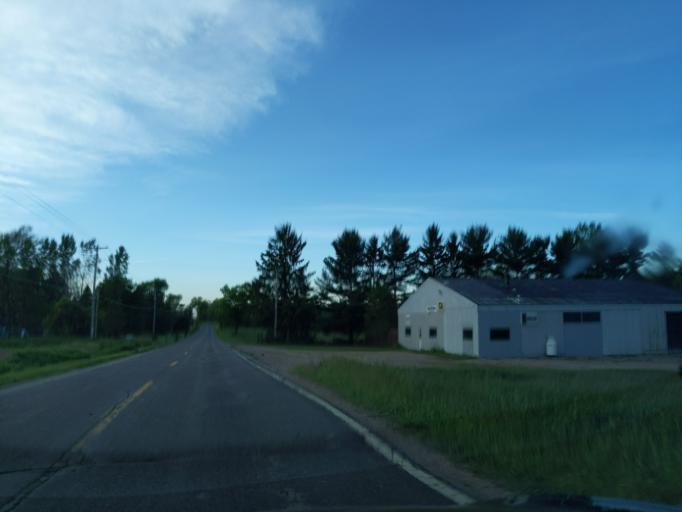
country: US
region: Michigan
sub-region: Ingham County
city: Mason
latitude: 42.5372
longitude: -84.3026
